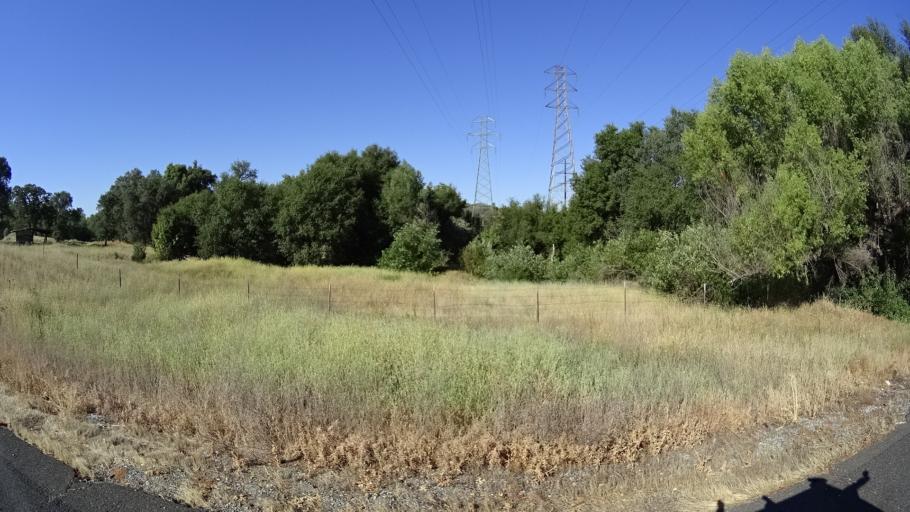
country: US
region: California
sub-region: Calaveras County
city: Murphys
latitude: 38.0942
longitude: -120.4684
